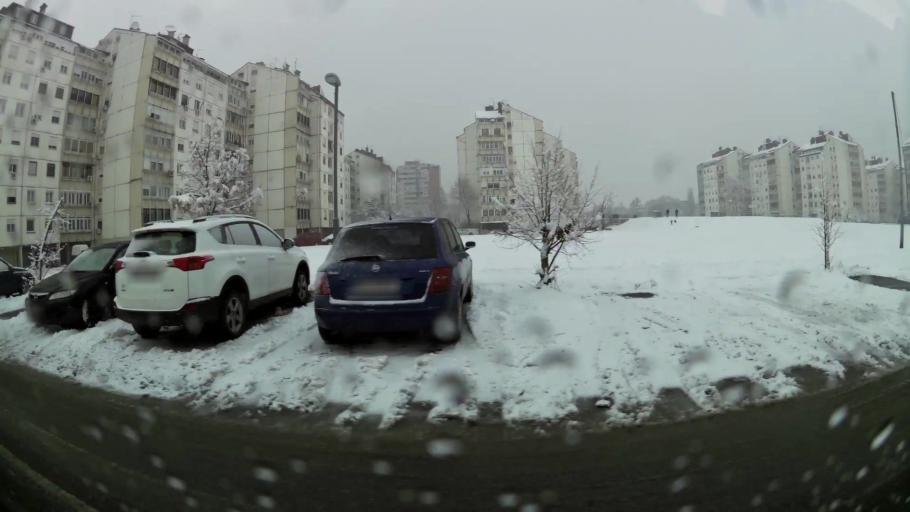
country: RS
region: Central Serbia
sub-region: Belgrade
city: Cukarica
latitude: 44.7947
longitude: 20.3705
